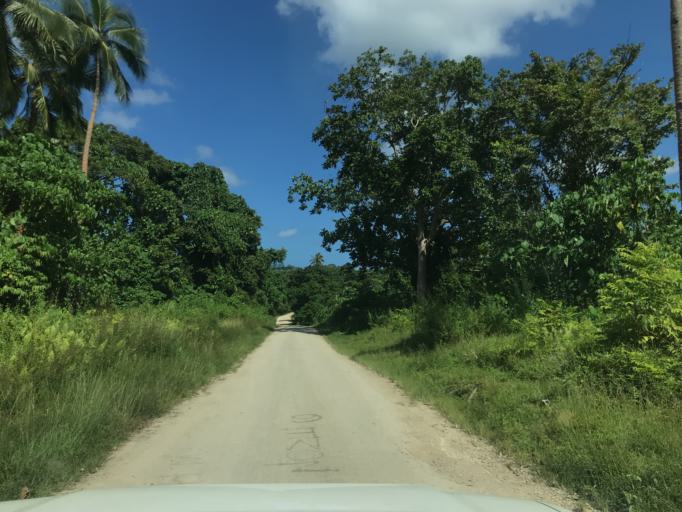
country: VU
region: Sanma
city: Luganville
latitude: -15.5776
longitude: 167.0380
